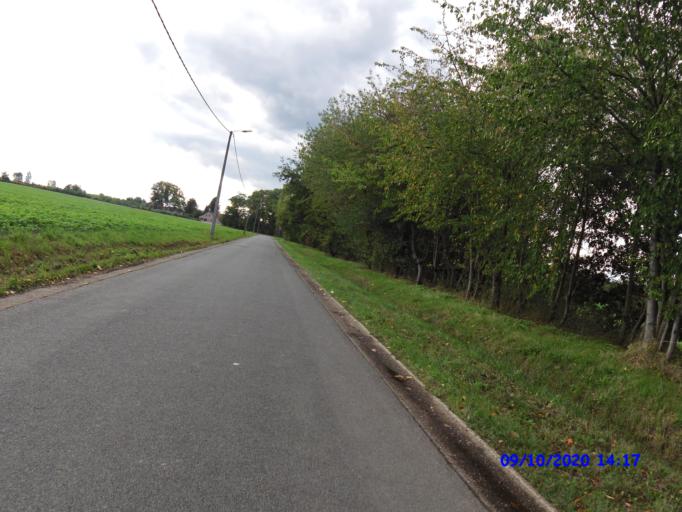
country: BE
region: Flanders
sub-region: Provincie Limburg
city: Nieuwerkerken
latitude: 50.8354
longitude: 5.2232
